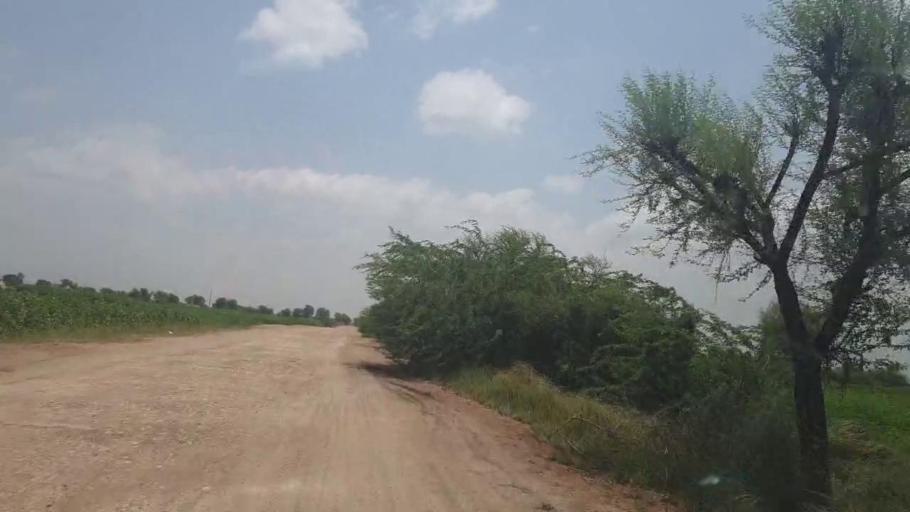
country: PK
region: Sindh
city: Tando Mittha Khan
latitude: 25.9177
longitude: 69.2116
